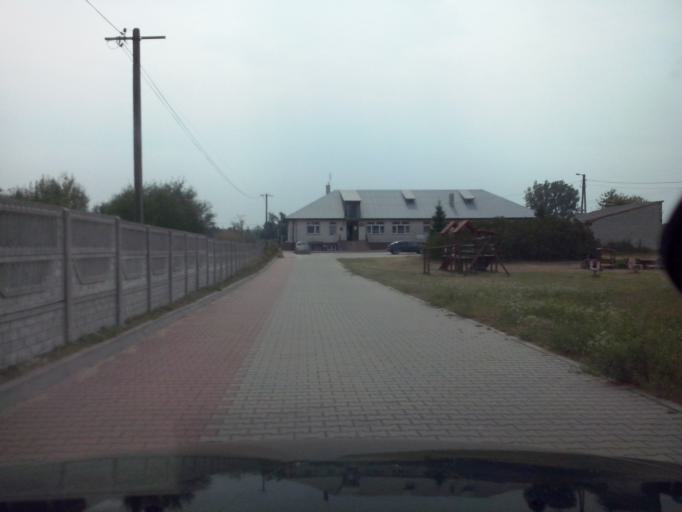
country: PL
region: Swietokrzyskie
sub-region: Powiat kielecki
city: Brzeziny
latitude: 50.7547
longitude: 20.5597
